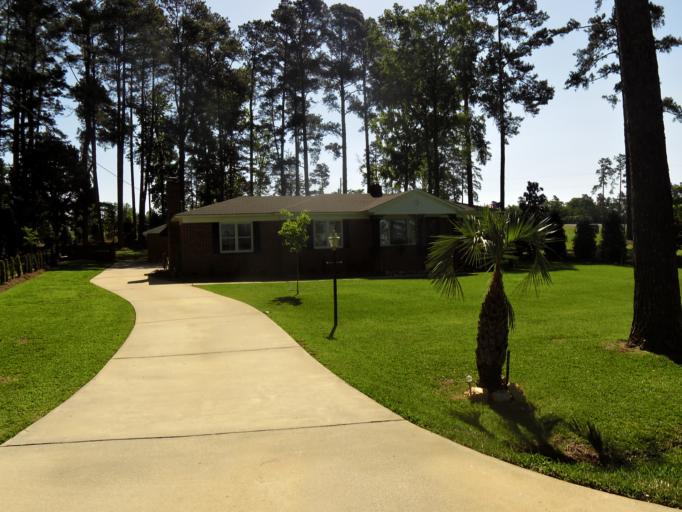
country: US
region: Georgia
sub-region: Columbia County
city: Martinez
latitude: 33.5072
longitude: -82.0294
